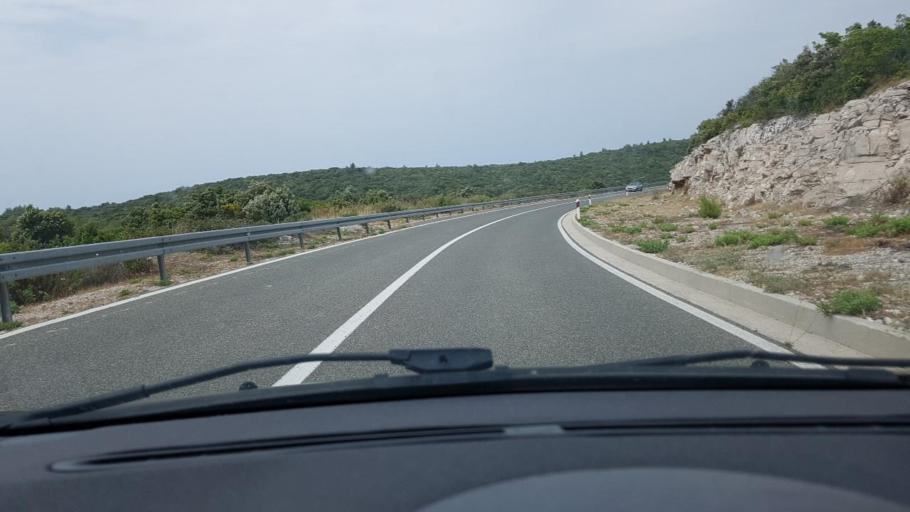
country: HR
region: Dubrovacko-Neretvanska
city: Smokvica
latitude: 42.9491
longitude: 16.9431
